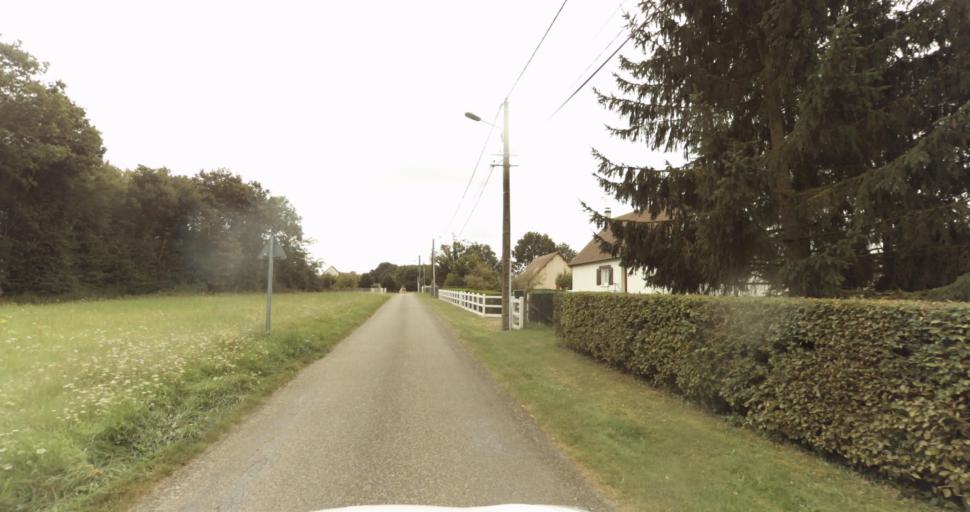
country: FR
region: Haute-Normandie
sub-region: Departement de l'Eure
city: La Madeleine-de-Nonancourt
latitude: 48.8367
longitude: 1.2161
